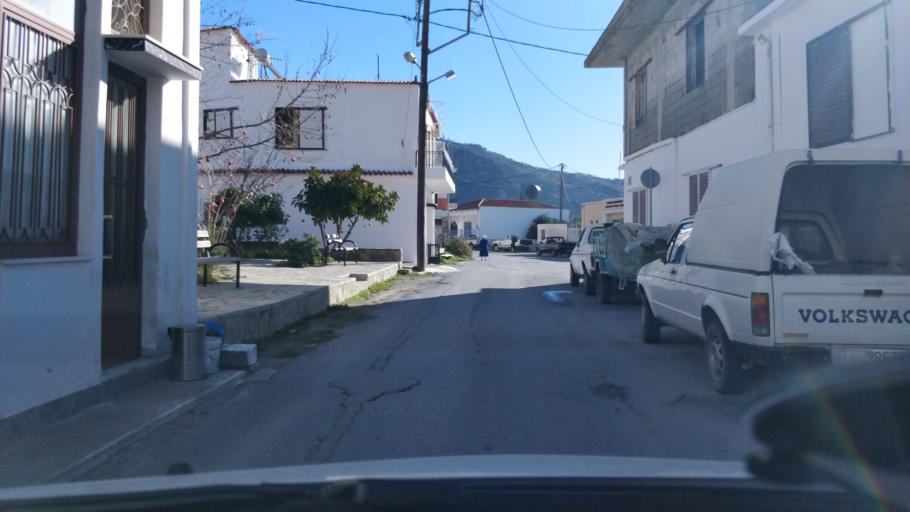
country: GR
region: Crete
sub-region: Nomos Lasithiou
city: Kritsa
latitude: 35.0799
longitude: 25.5873
